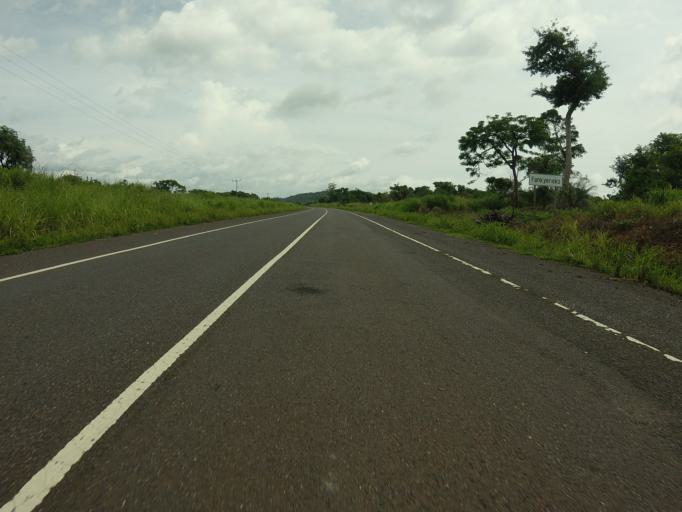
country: TG
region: Plateaux
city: Badou
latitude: 7.9577
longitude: 0.5552
